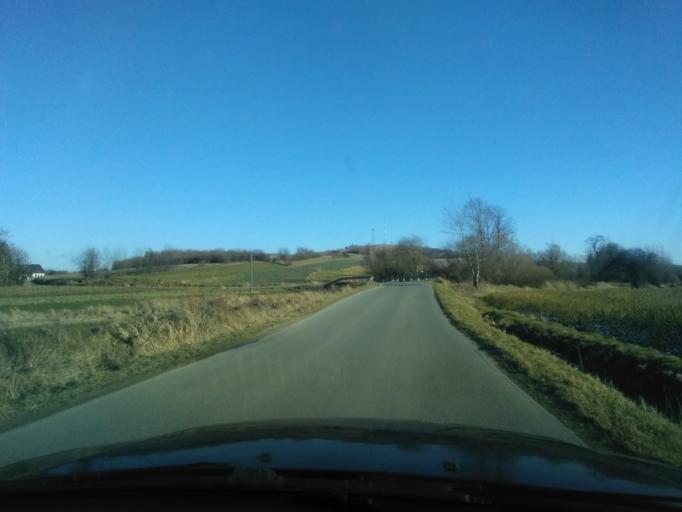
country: PL
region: Subcarpathian Voivodeship
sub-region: Powiat krosnienski
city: Rymanow
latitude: 49.5788
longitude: 21.8800
